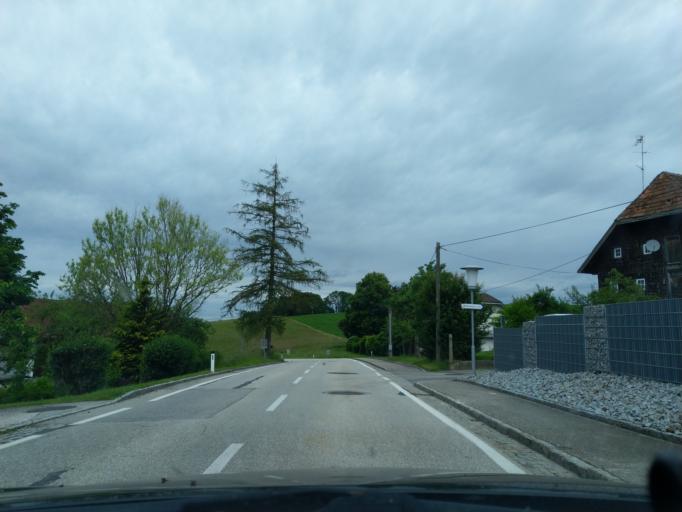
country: DE
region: Bavaria
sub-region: Lower Bavaria
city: Bad Fussing
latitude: 48.2837
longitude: 13.3604
